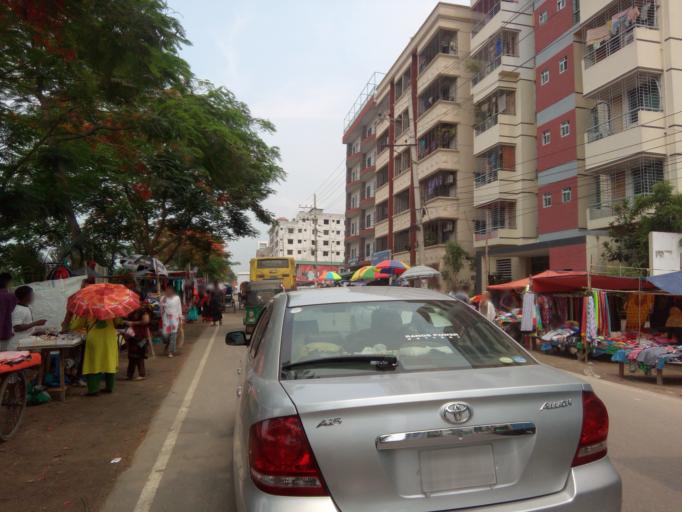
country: BD
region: Dhaka
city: Paltan
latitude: 23.7624
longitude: 90.4400
